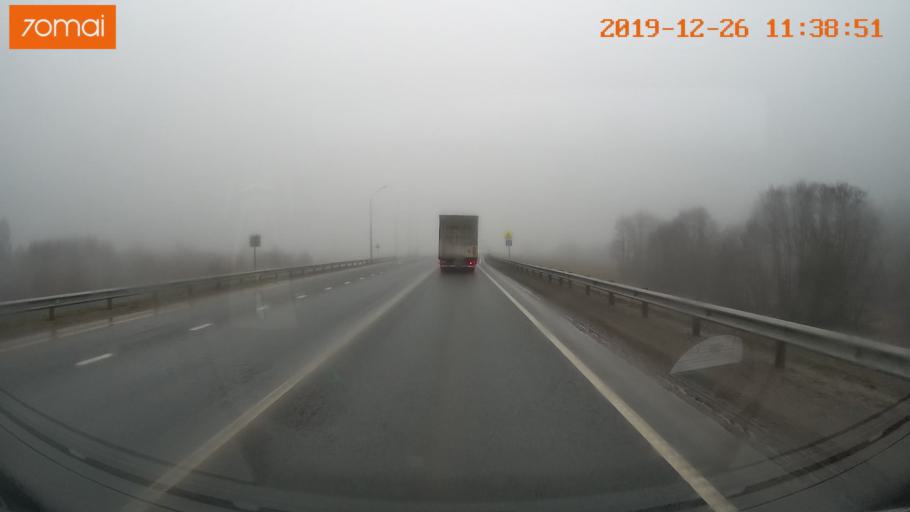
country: RU
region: Vologda
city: Sheksna
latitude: 59.2110
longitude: 38.6123
